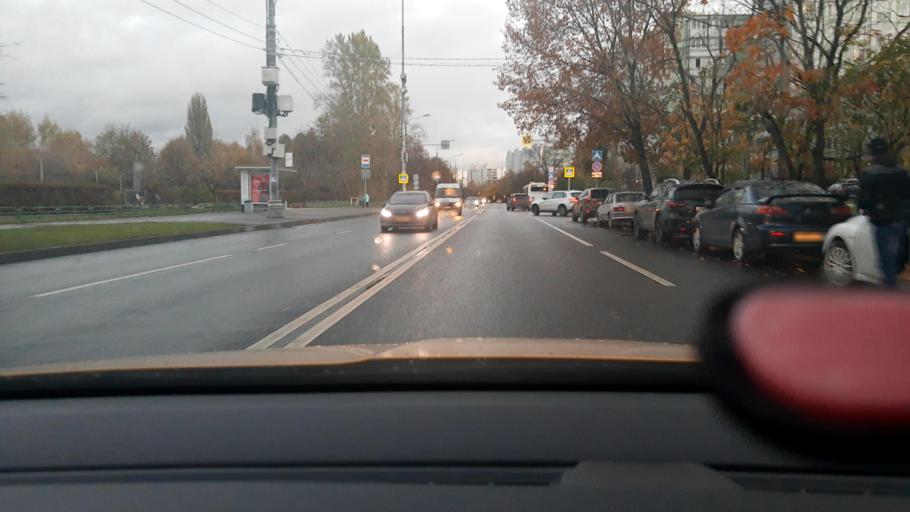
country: RU
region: Moscow
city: Strogino
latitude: 55.8135
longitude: 37.4093
